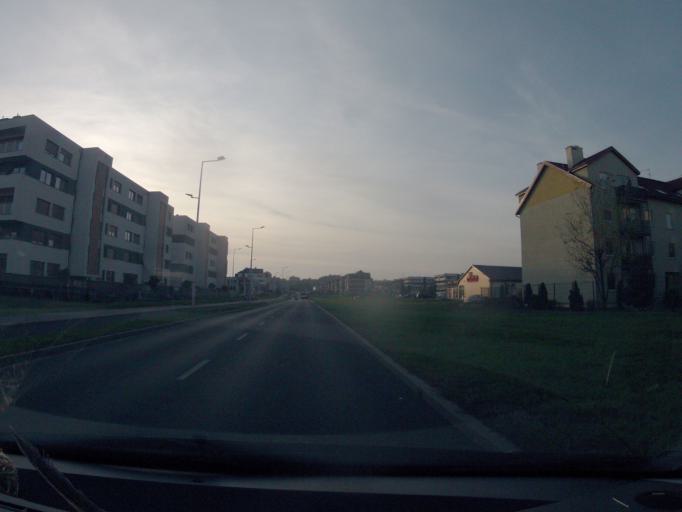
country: PL
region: Opole Voivodeship
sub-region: Powiat opolski
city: Opole
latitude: 50.6754
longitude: 17.9728
